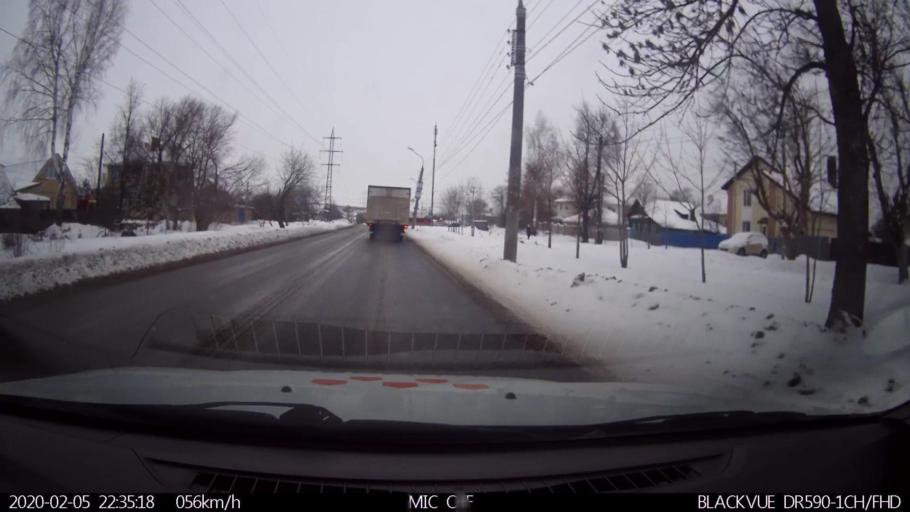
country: RU
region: Nizjnij Novgorod
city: Imeni Stepana Razina
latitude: 54.7350
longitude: 44.2376
